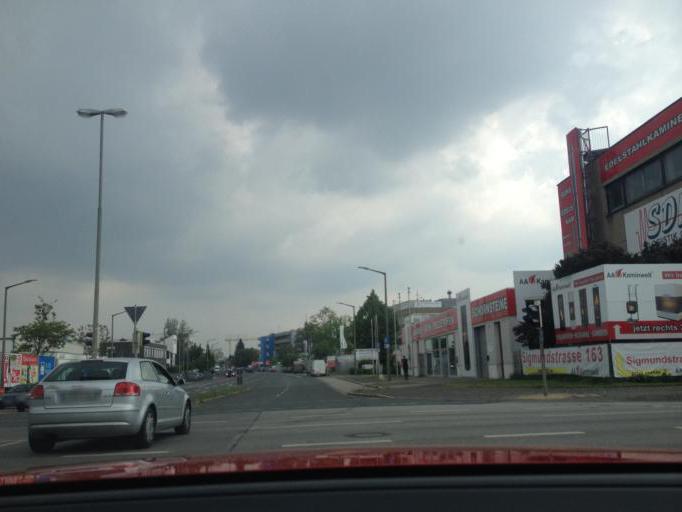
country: DE
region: Bavaria
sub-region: Regierungsbezirk Mittelfranken
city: Grossreuth bei Schweinau
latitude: 49.4460
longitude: 11.0083
